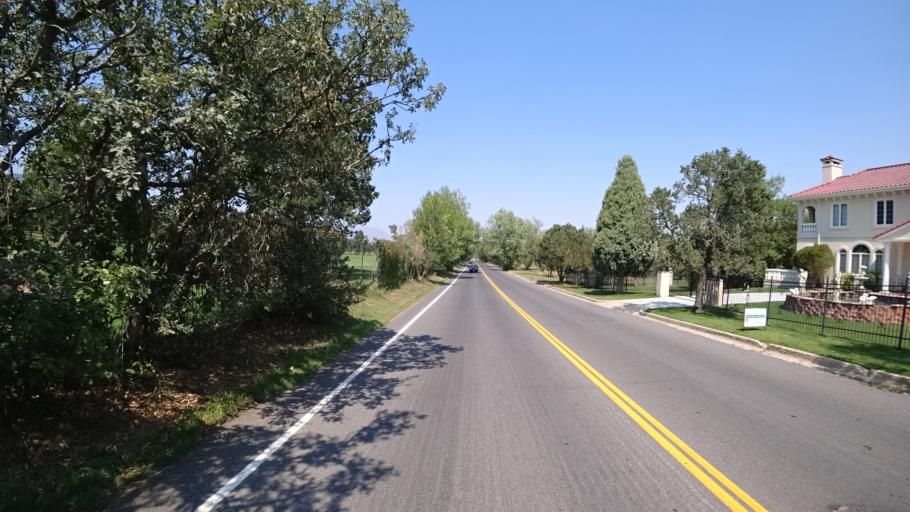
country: US
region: Colorado
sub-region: El Paso County
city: Colorado Springs
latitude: 38.7831
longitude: -104.8455
